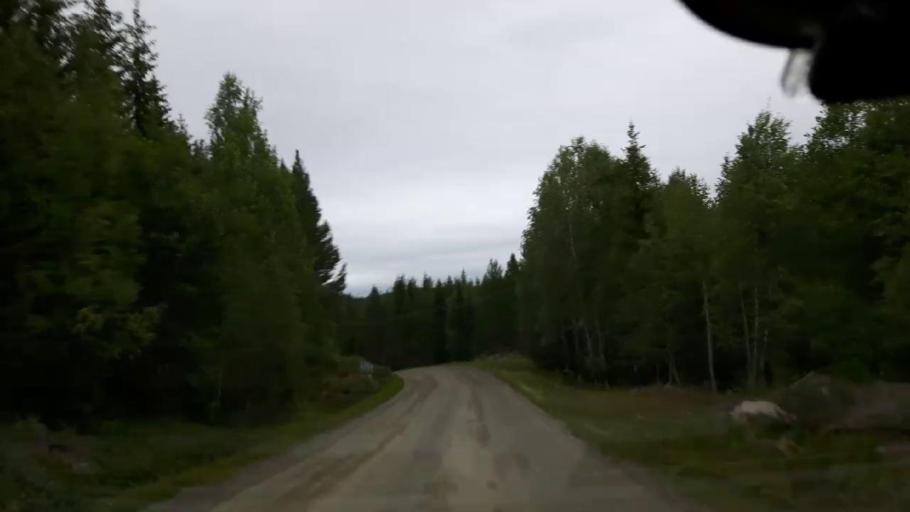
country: SE
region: Vaesternorrland
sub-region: Ange Kommun
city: Fransta
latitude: 62.8589
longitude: 15.9826
